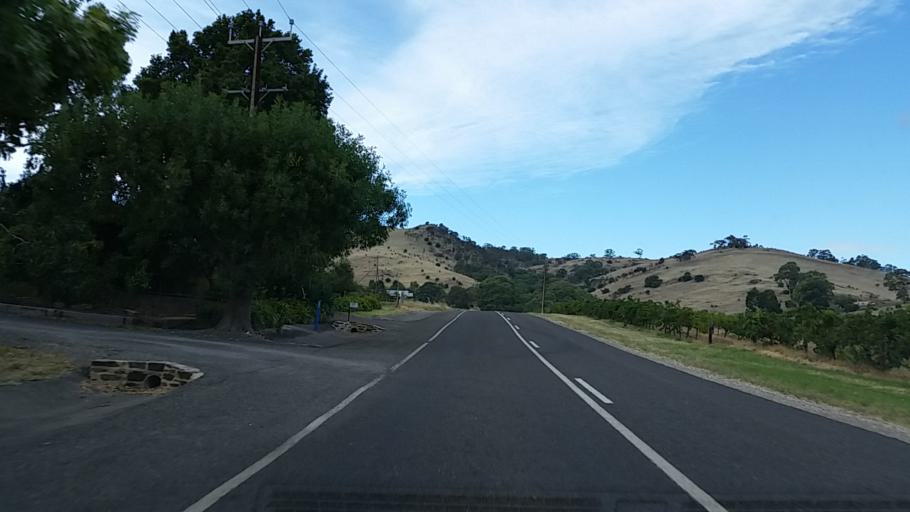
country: AU
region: South Australia
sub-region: Barossa
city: Tanunda
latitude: -34.5430
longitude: 138.9862
